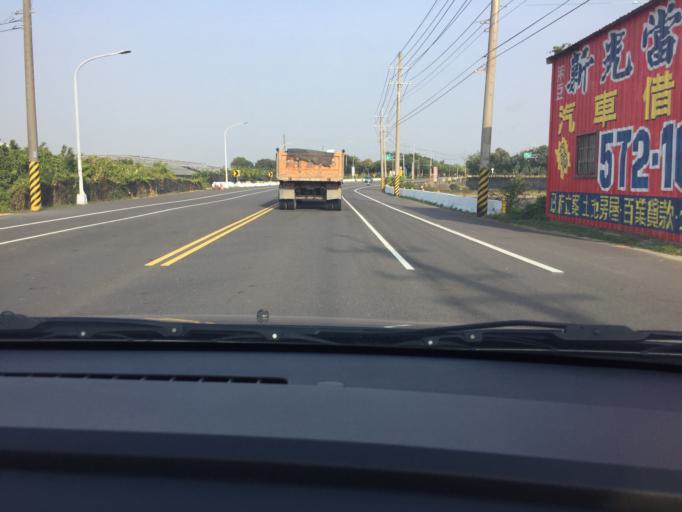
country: TW
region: Taiwan
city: Xinying
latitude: 23.1994
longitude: 120.2919
